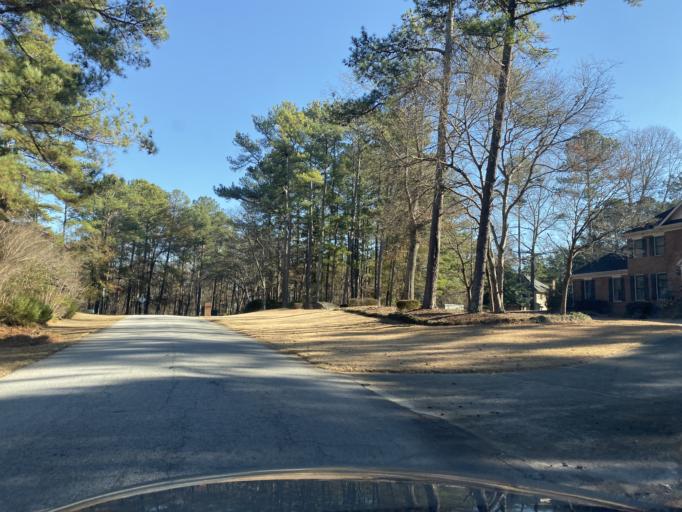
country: US
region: Georgia
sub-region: DeKalb County
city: Pine Mountain
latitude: 33.6792
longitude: -84.1647
